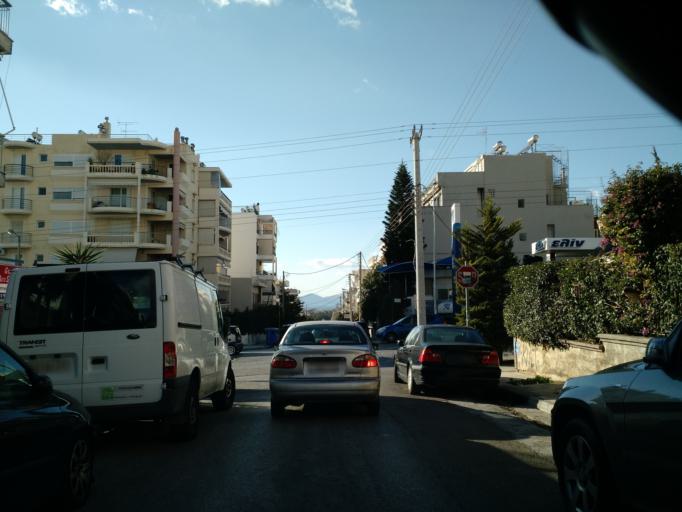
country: GR
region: Attica
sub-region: Nomarchia Athinas
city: Argyroupoli
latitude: 37.9168
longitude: 23.7507
